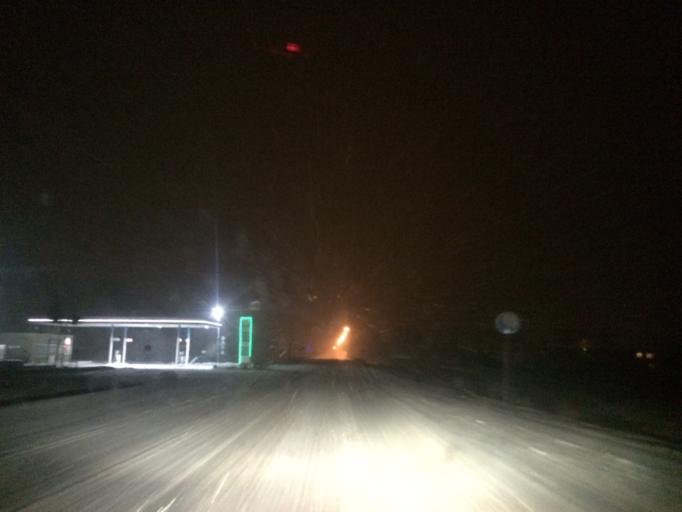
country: RU
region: Tula
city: Dubna
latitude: 54.0988
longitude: 37.1027
